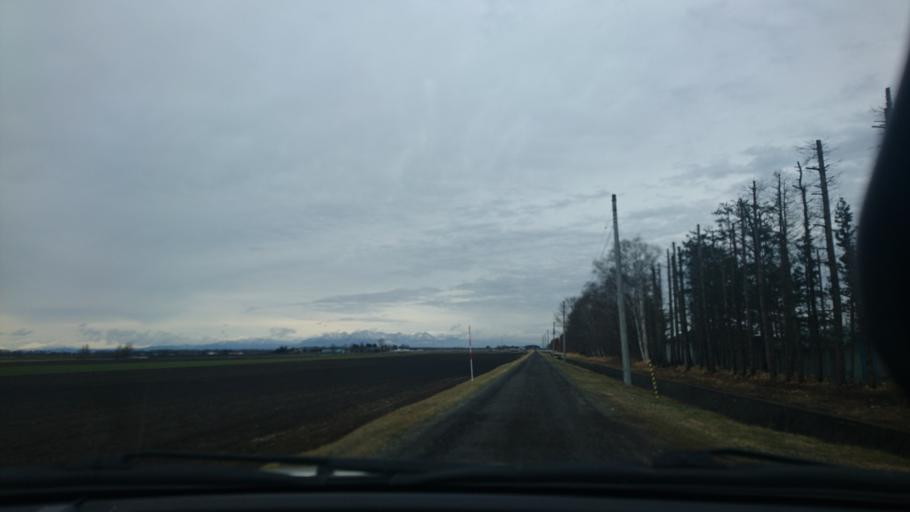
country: JP
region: Hokkaido
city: Otofuke
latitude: 43.0307
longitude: 143.2251
